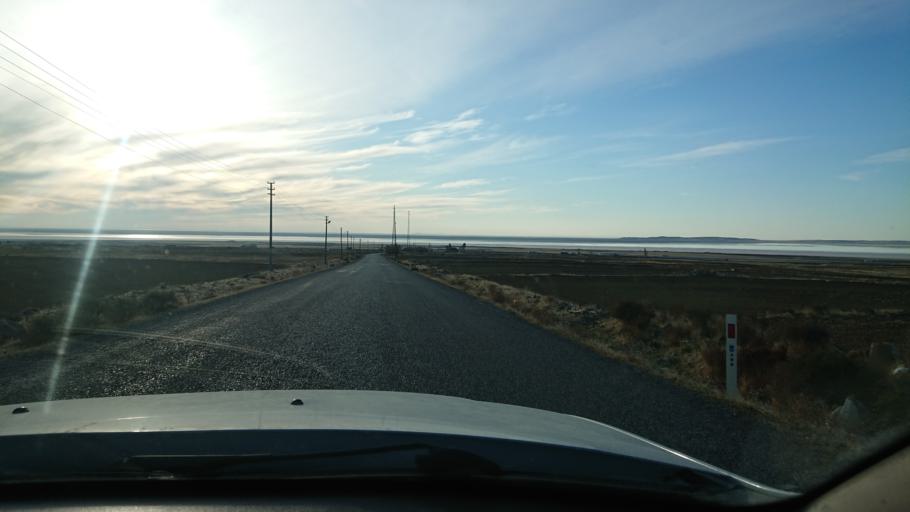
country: TR
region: Ankara
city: Sereflikochisar
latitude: 38.7442
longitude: 33.6770
